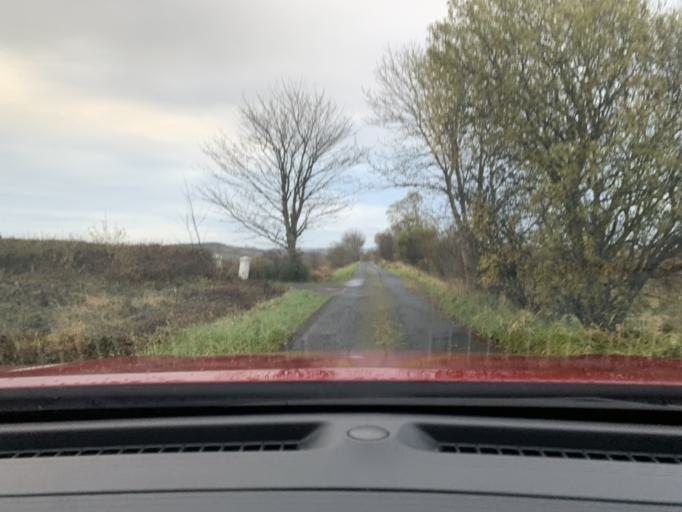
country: IE
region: Connaught
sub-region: Sligo
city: Ballymote
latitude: 54.0174
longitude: -8.5193
